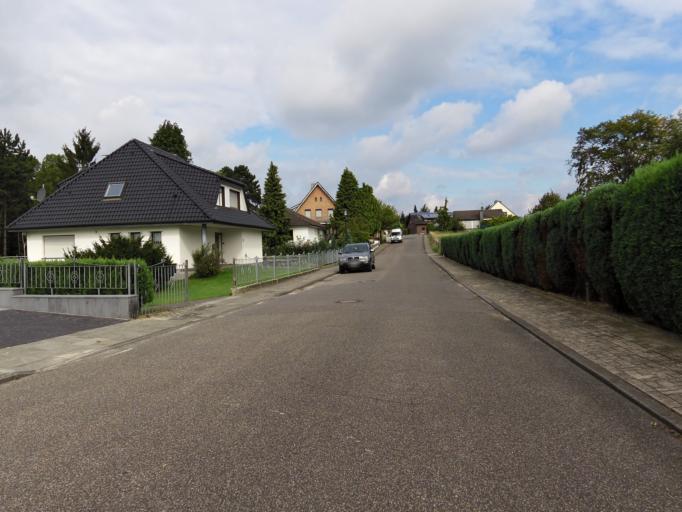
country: DE
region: North Rhine-Westphalia
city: Geilenkirchen
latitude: 50.9548
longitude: 6.0783
